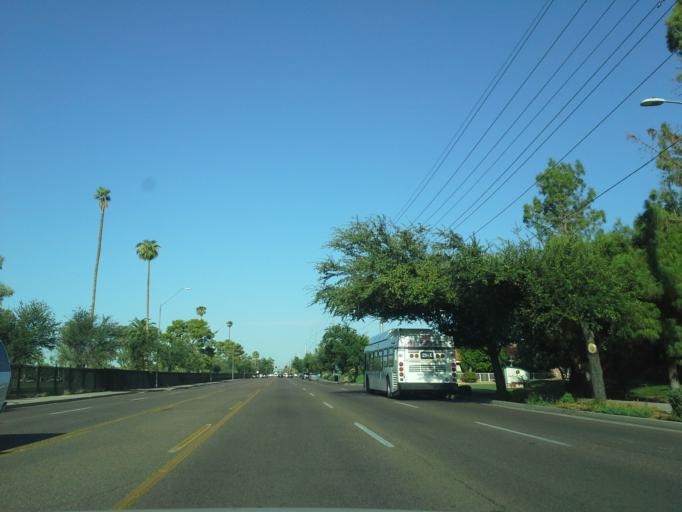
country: US
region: Arizona
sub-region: Maricopa County
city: Phoenix
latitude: 33.4805
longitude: -112.0949
